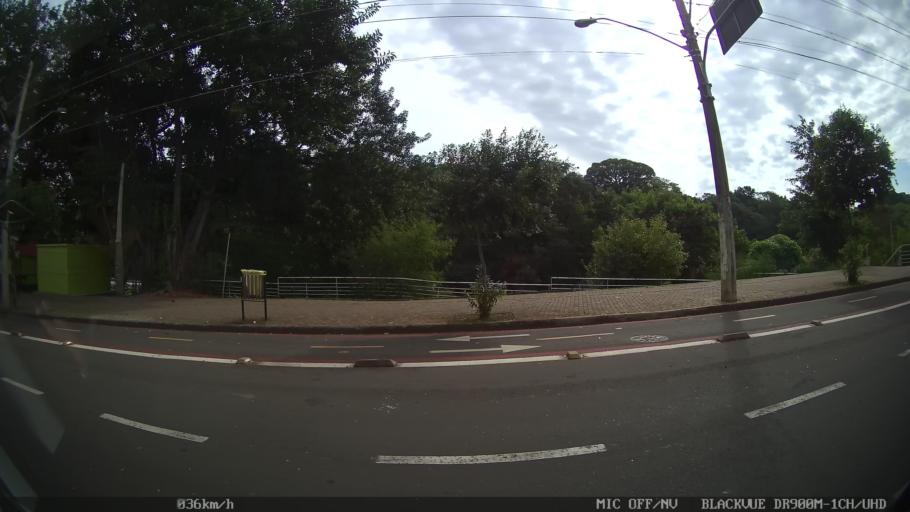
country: BR
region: Sao Paulo
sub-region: Piracicaba
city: Piracicaba
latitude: -22.7174
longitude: -47.6530
